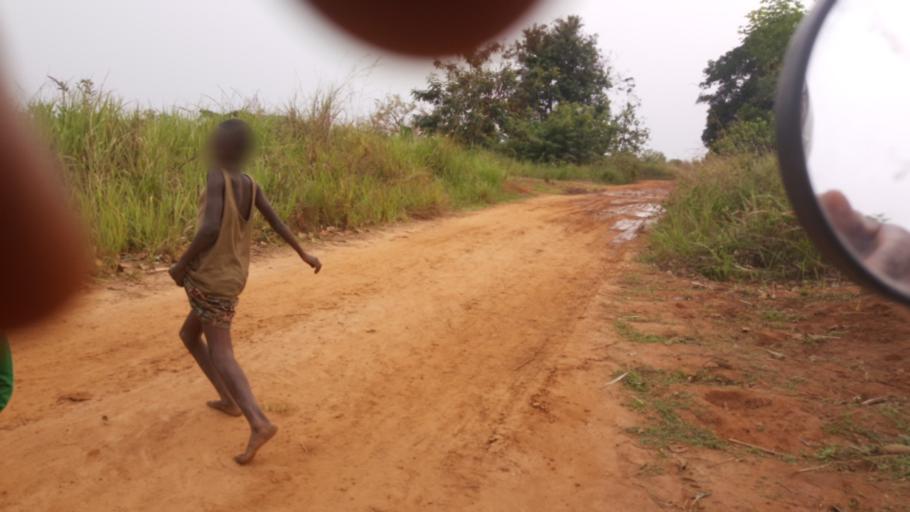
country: CD
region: Bandundu
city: Bandundu
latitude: -3.4651
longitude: 17.7158
